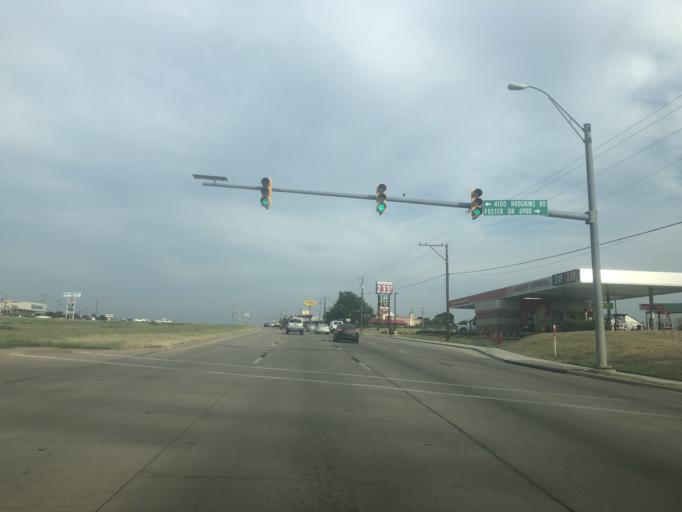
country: US
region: Texas
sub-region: Tarrant County
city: Lake Worth
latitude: 32.8155
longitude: -97.4400
